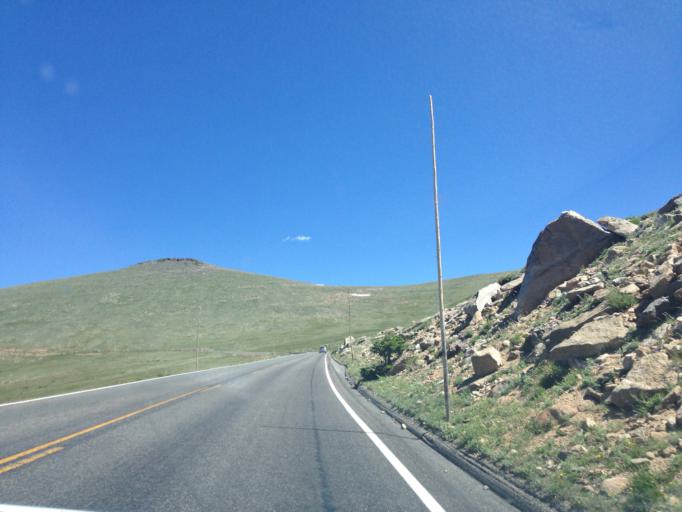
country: US
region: Colorado
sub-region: Larimer County
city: Estes Park
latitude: 40.3989
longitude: -105.7104
